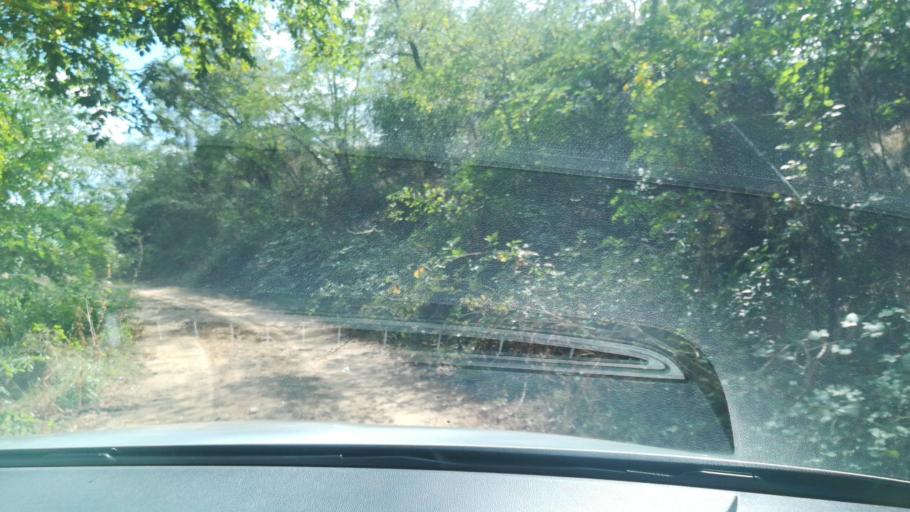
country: MK
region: Delcevo
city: Delcevo
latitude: 41.8921
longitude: 22.8046
